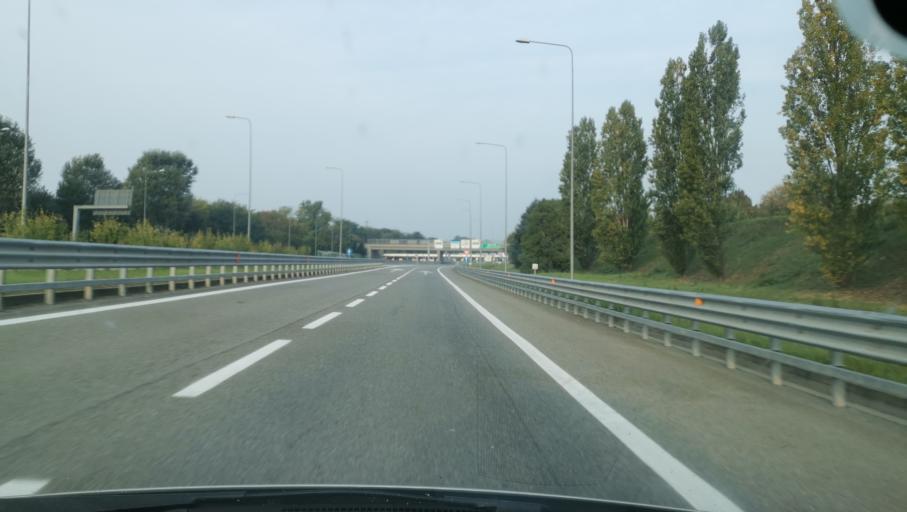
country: IT
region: Piedmont
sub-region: Provincia di Torino
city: Rivoli
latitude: 45.0811
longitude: 7.5460
